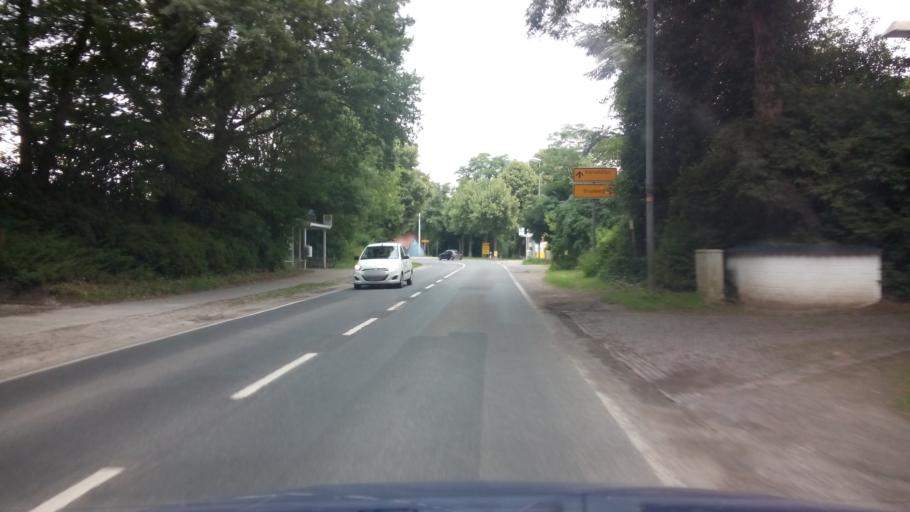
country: DE
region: Lower Saxony
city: Worpswede
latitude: 53.2186
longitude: 8.9341
